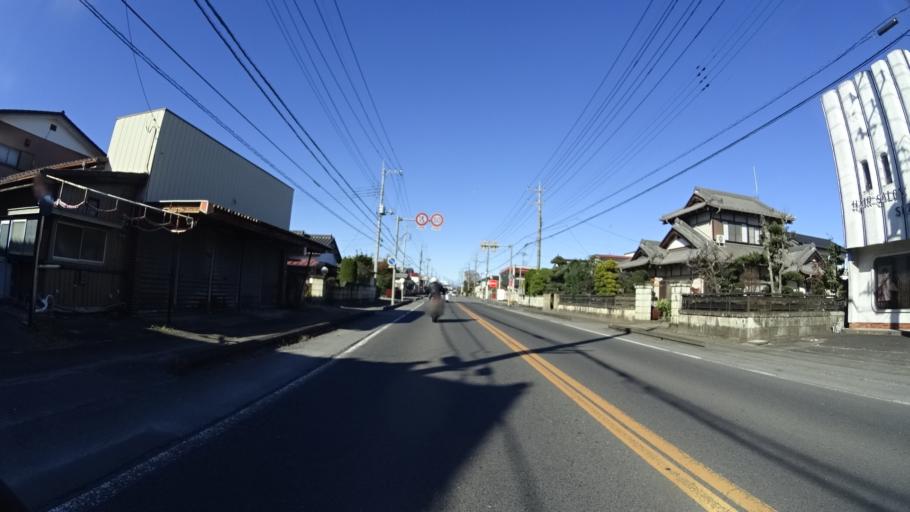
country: JP
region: Tochigi
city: Kanuma
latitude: 36.5198
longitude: 139.7512
